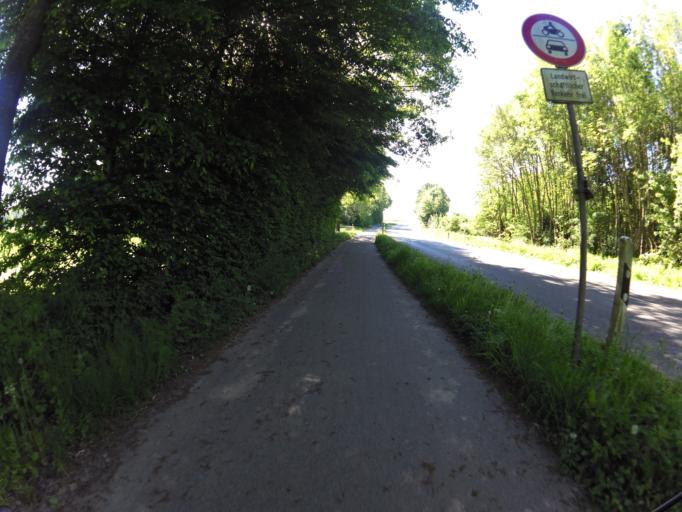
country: DE
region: North Rhine-Westphalia
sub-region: Regierungsbezirk Koln
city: Linnich
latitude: 50.9426
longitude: 6.2635
